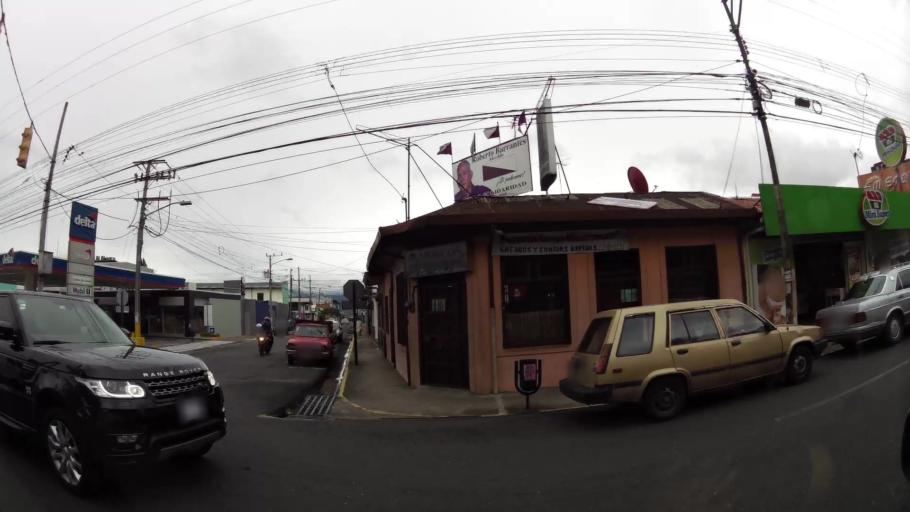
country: CR
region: San Jose
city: San Jose
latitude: 9.9319
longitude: -84.0948
